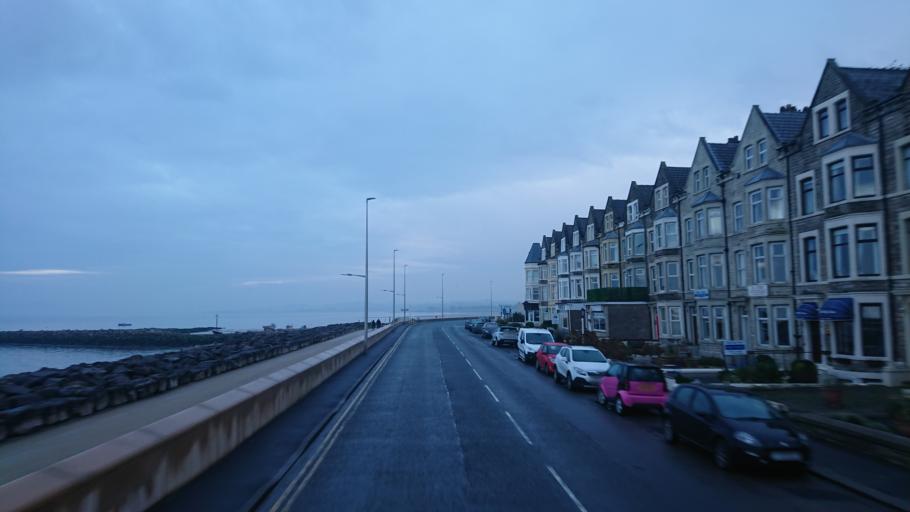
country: GB
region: England
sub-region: Lancashire
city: Morecambe
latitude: 54.0769
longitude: -2.8586
